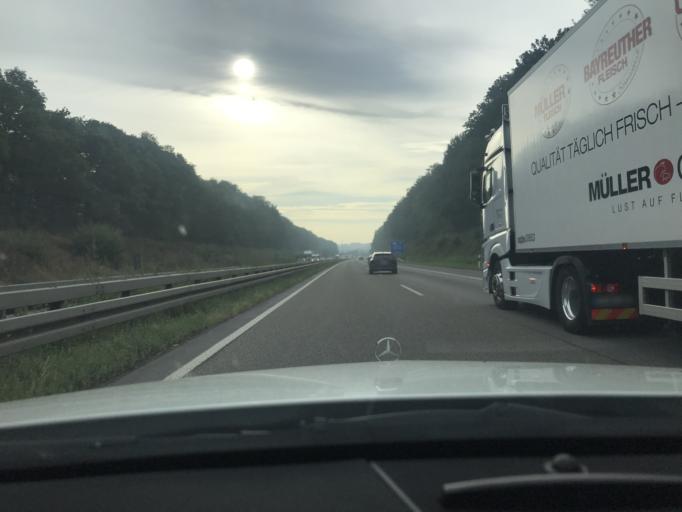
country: DE
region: Hesse
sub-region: Regierungsbezirk Giessen
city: Hoernsheim
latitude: 50.5278
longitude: 8.6075
